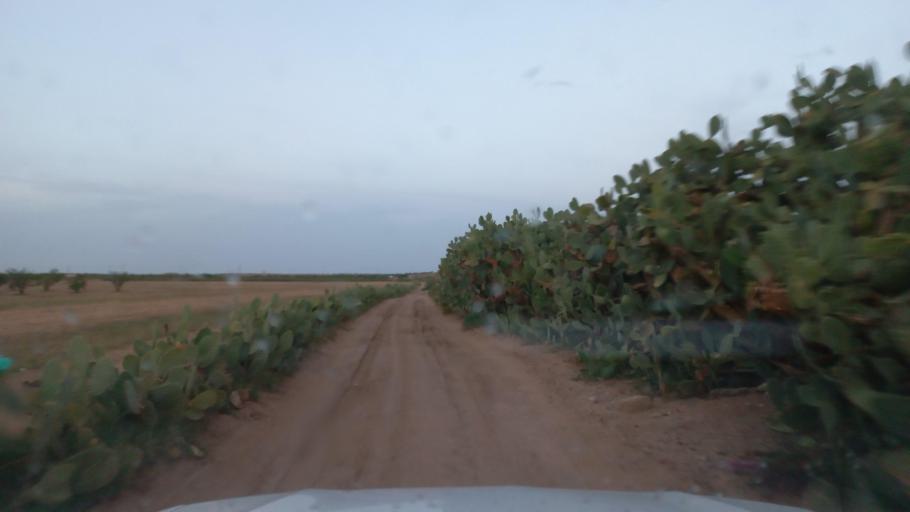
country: TN
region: Al Qasrayn
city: Sbiba
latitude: 35.3521
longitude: 9.0425
